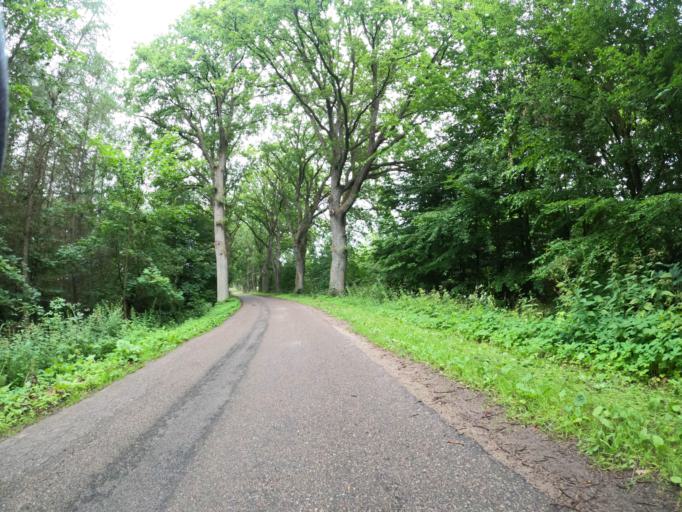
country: PL
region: West Pomeranian Voivodeship
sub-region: Powiat koszalinski
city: Bobolice
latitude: 53.9189
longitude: 16.5001
